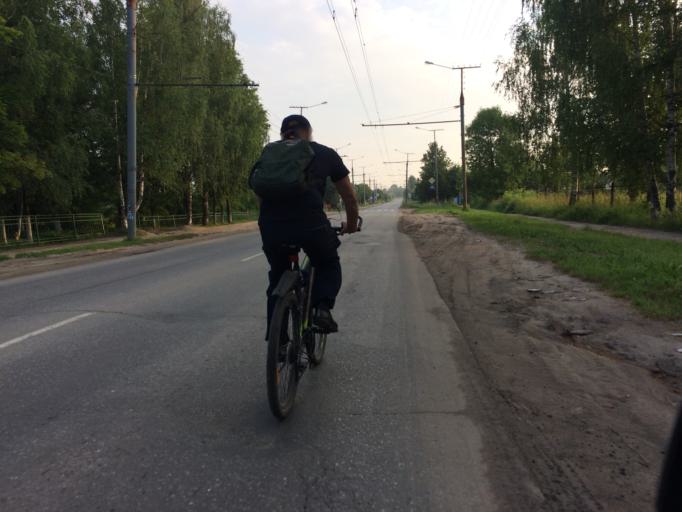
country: RU
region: Mariy-El
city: Yoshkar-Ola
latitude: 56.6415
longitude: 47.9540
